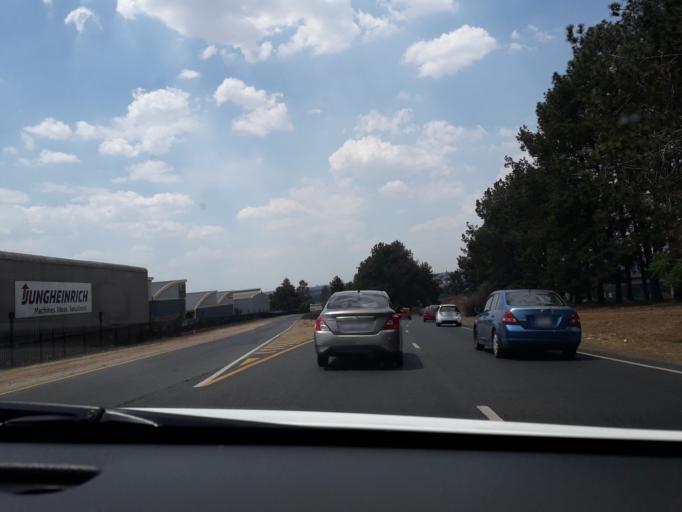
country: ZA
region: Gauteng
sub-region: City of Johannesburg Metropolitan Municipality
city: Modderfontein
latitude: -26.1115
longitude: 28.1445
